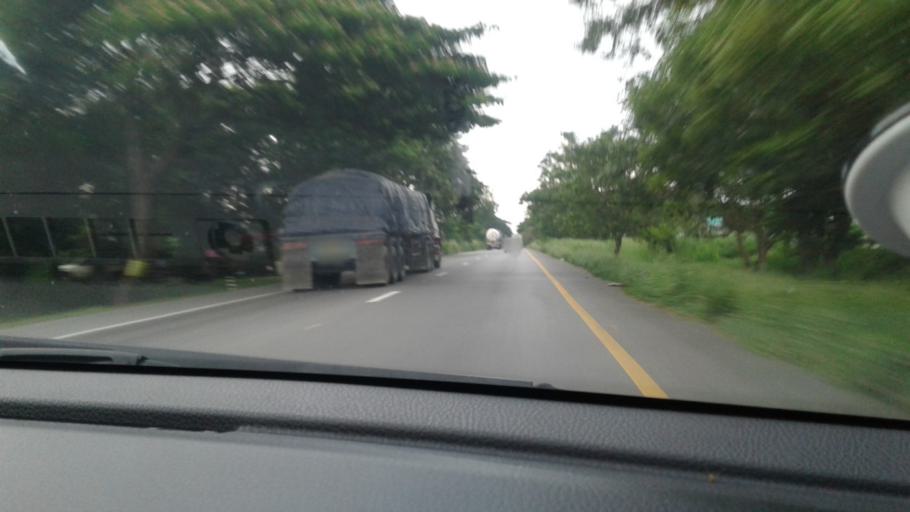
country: TH
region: Prachuap Khiri Khan
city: Hua Hin
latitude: 12.5197
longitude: 99.8816
